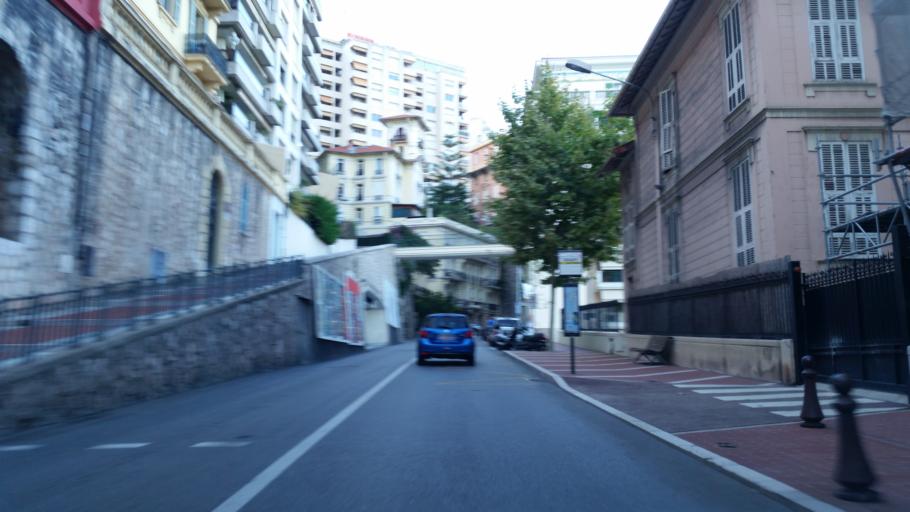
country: MC
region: Commune de Monaco
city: Moneghetti
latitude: 43.7352
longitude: 7.4172
